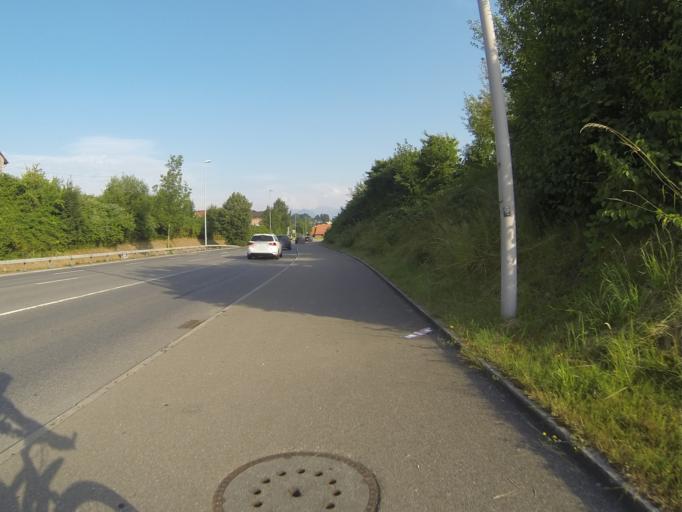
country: CH
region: Lucerne
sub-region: Lucerne-Stadt District
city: Luzern
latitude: 47.0673
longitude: 8.2959
